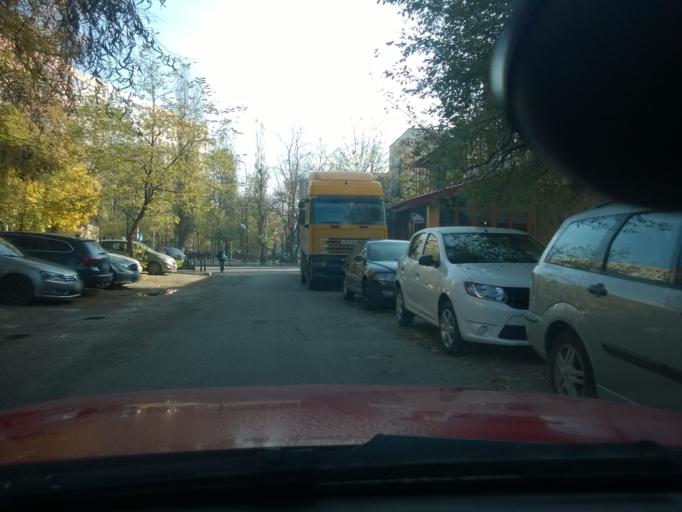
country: RO
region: Ilfov
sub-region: Comuna Popesti-Leordeni
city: Popesti-Leordeni
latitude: 44.4139
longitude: 26.1783
